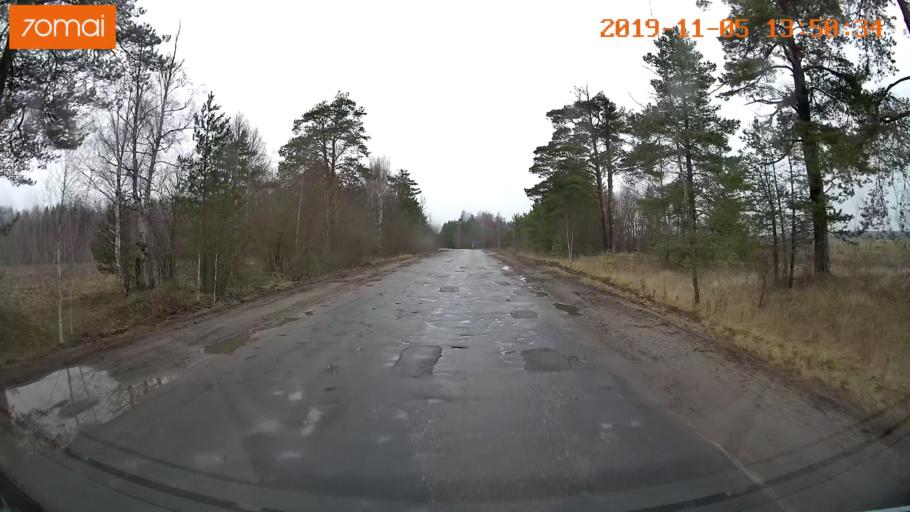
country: RU
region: Ivanovo
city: Kaminskiy
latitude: 57.0202
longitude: 41.4074
